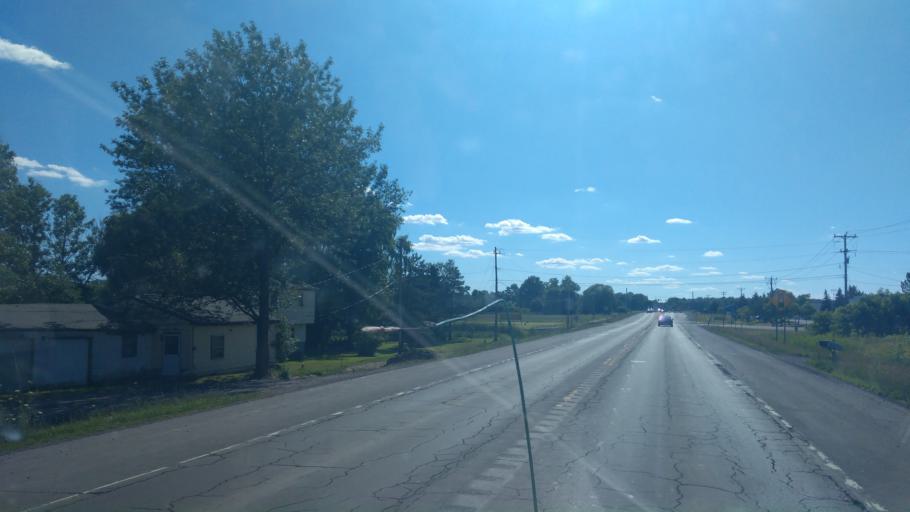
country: US
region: New York
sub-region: Seneca County
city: Waterloo
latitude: 42.9544
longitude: -76.9169
